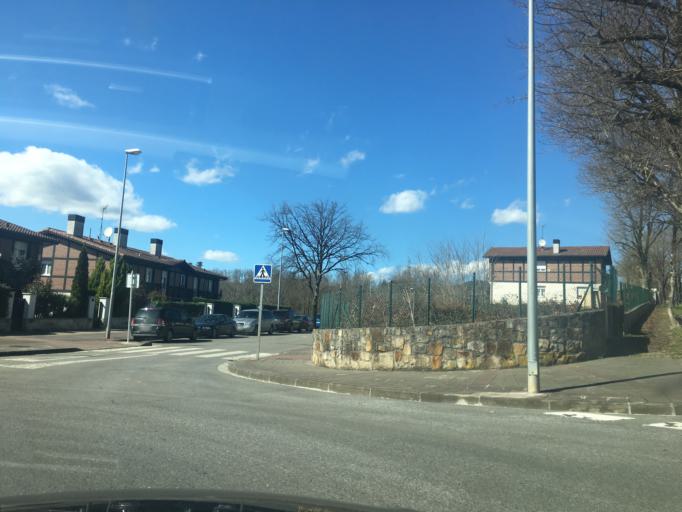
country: ES
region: Basque Country
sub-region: Bizkaia
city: Amorebieta
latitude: 43.2307
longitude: -2.7387
